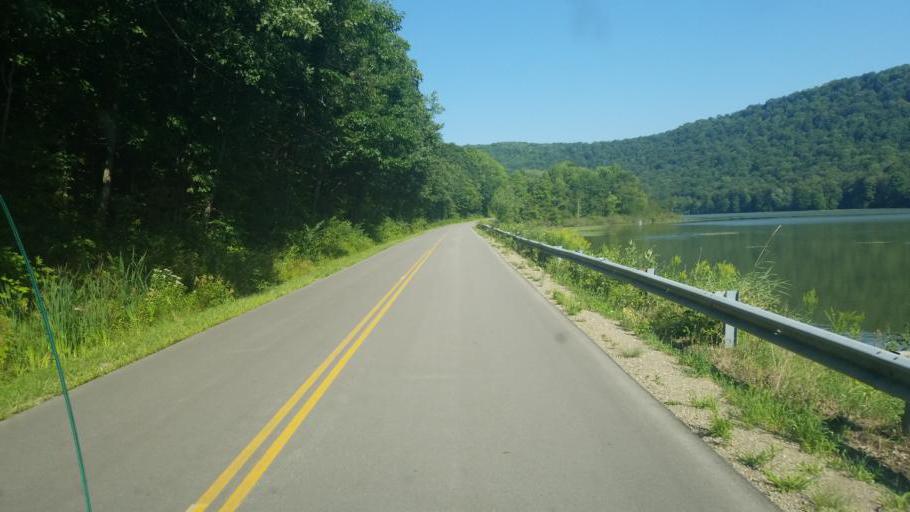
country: US
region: New York
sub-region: Allegany County
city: Wellsville
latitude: 42.0155
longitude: -77.9997
